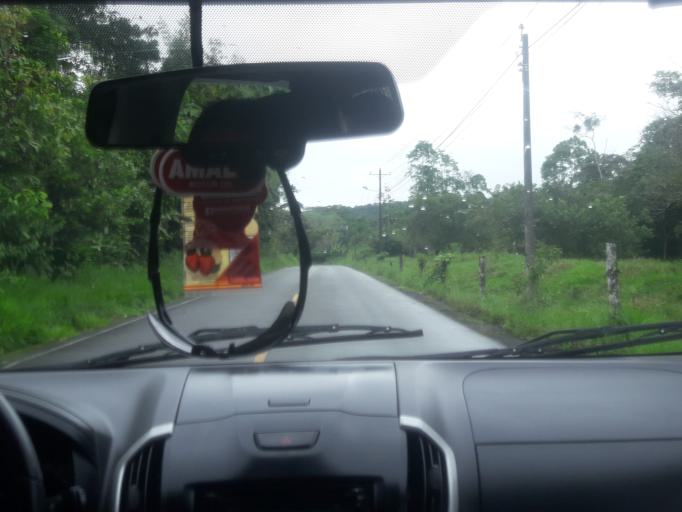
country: EC
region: Napo
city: Tena
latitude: -1.0337
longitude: -77.6846
